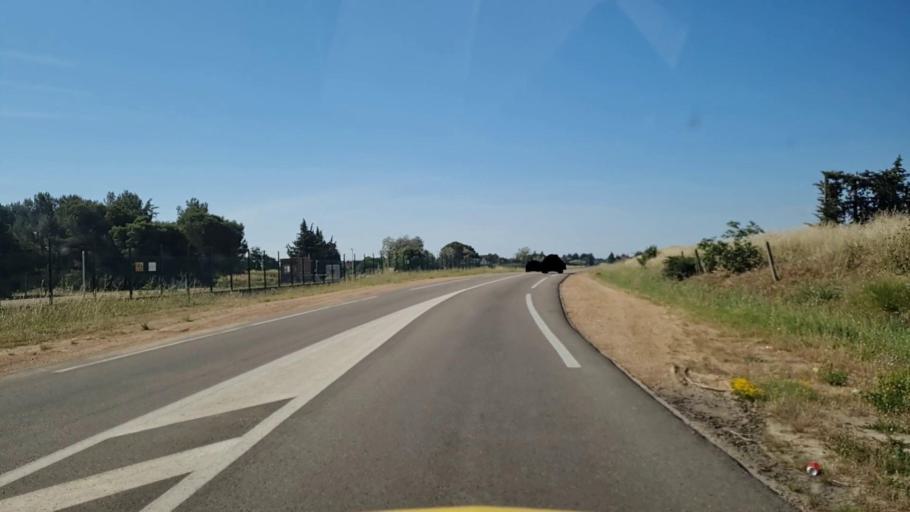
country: FR
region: Languedoc-Roussillon
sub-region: Departement du Gard
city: Garons
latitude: 43.7708
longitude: 4.4051
